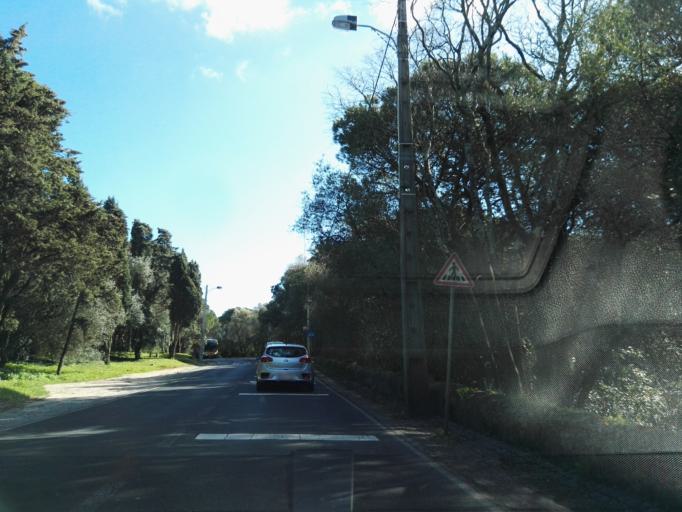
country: PT
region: Lisbon
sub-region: Odivelas
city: Pontinha
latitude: 38.7294
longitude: -9.1979
